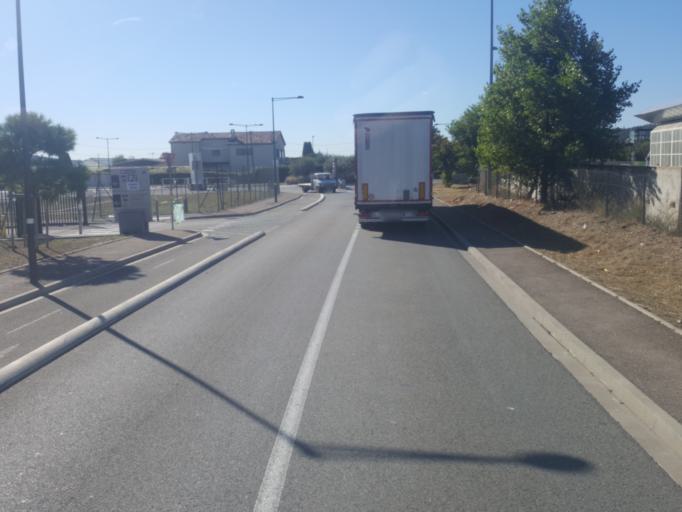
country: FR
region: Provence-Alpes-Cote d'Azur
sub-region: Departement des Alpes-Maritimes
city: Saint-Laurent-du-Var
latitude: 43.7050
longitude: 7.1906
